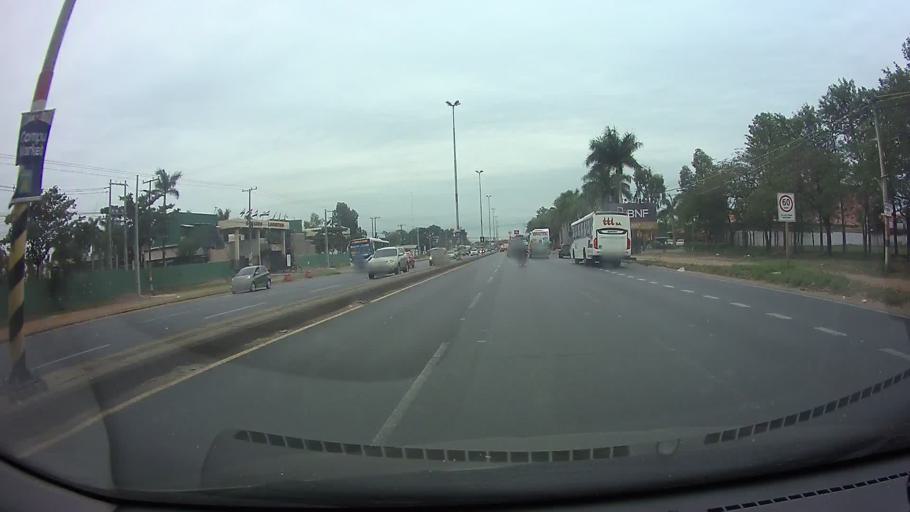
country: PY
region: Central
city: Colonia Mariano Roque Alonso
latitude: -25.2307
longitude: -57.5367
